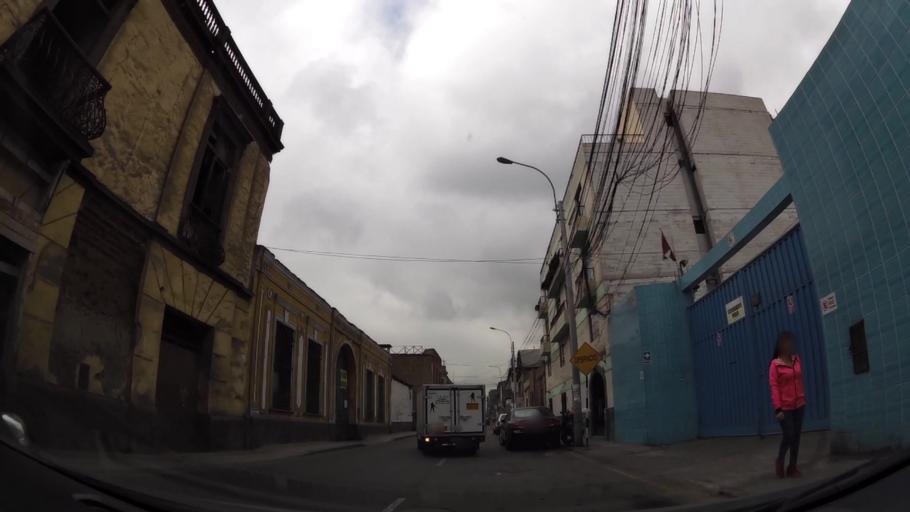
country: PE
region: Lima
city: Lima
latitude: -12.0414
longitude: -77.0388
